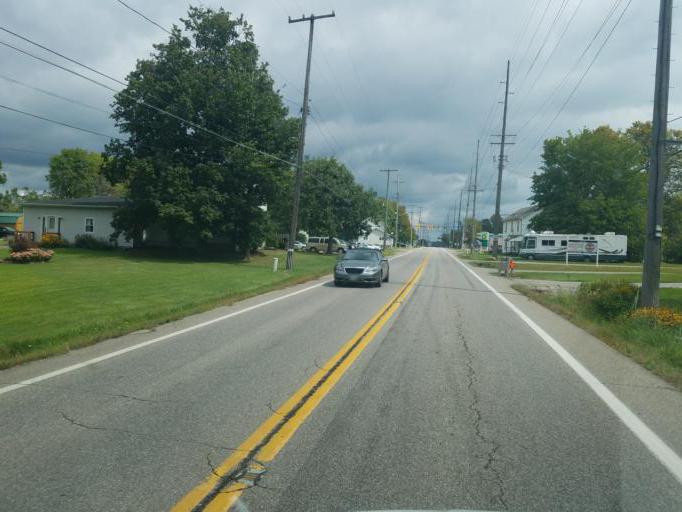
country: US
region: Ohio
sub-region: Geauga County
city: Burton
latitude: 41.5323
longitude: -81.1174
